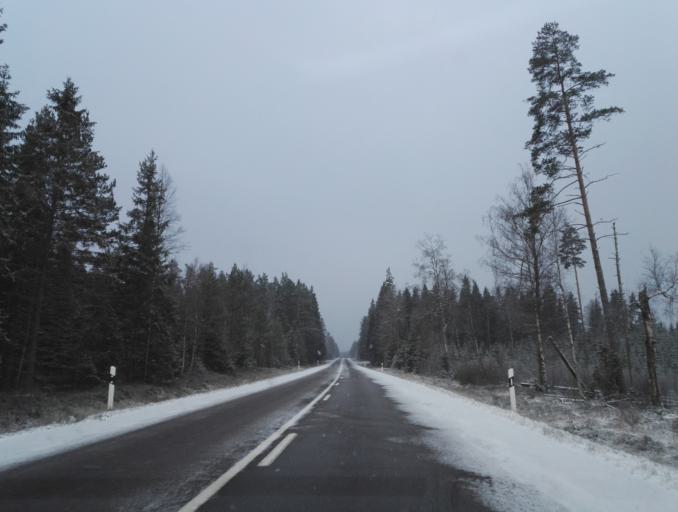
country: SE
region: Kronoberg
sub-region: Uppvidinge Kommun
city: Lenhovda
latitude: 56.9011
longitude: 15.3680
